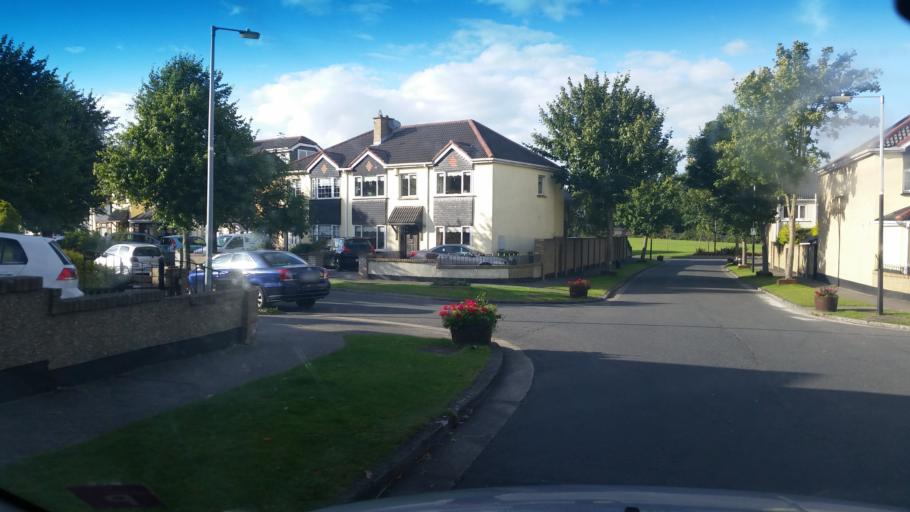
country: IE
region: Leinster
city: Beaumont
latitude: 53.4006
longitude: -6.2310
